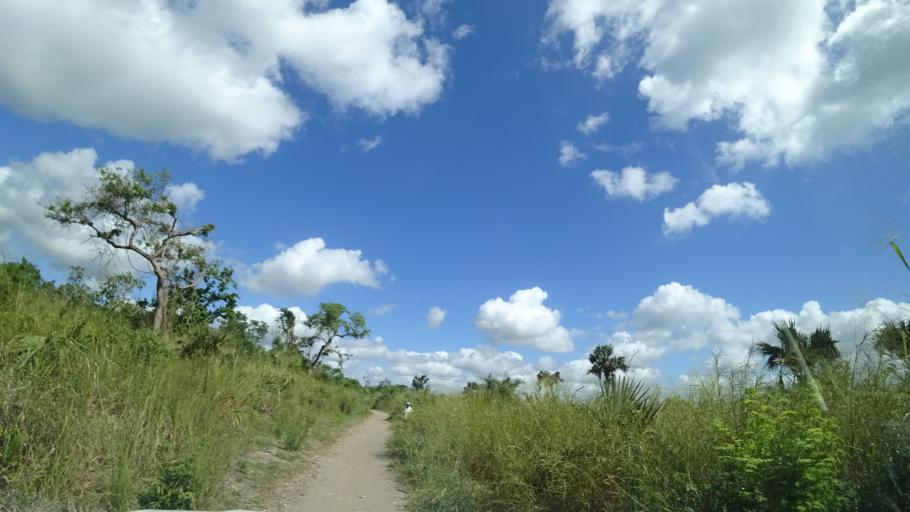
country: MZ
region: Sofala
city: Dondo
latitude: -19.3590
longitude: 34.5779
